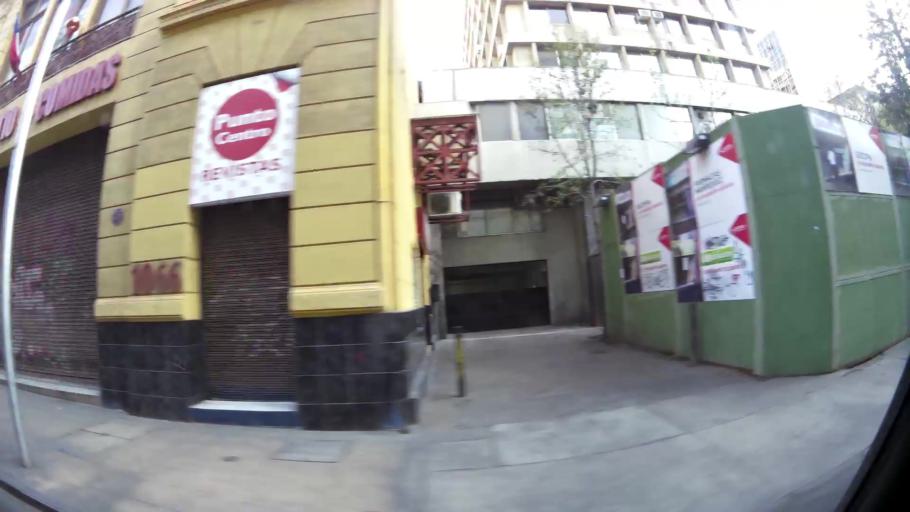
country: CL
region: Santiago Metropolitan
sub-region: Provincia de Santiago
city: Santiago
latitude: -33.4364
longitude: -70.6524
